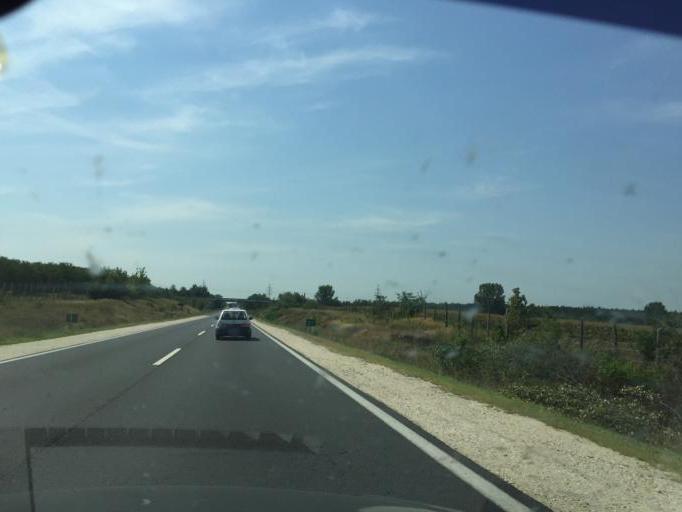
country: HU
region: Pest
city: God
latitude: 47.6704
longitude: 19.1675
